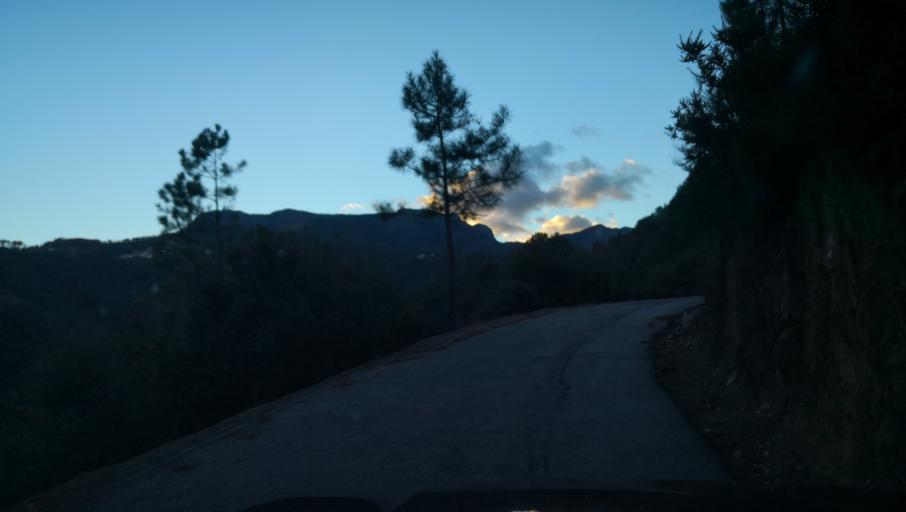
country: PT
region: Vila Real
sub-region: Santa Marta de Penaguiao
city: Santa Marta de Penaguiao
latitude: 41.2585
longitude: -7.8243
